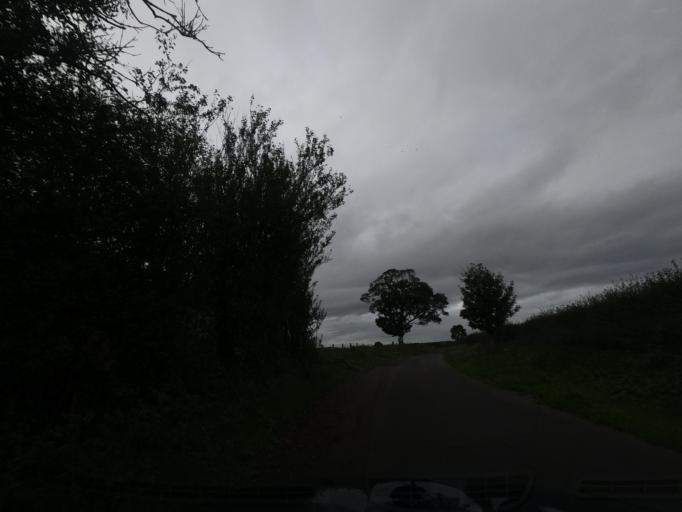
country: GB
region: England
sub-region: Northumberland
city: Doddington
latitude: 55.5881
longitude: -2.0088
